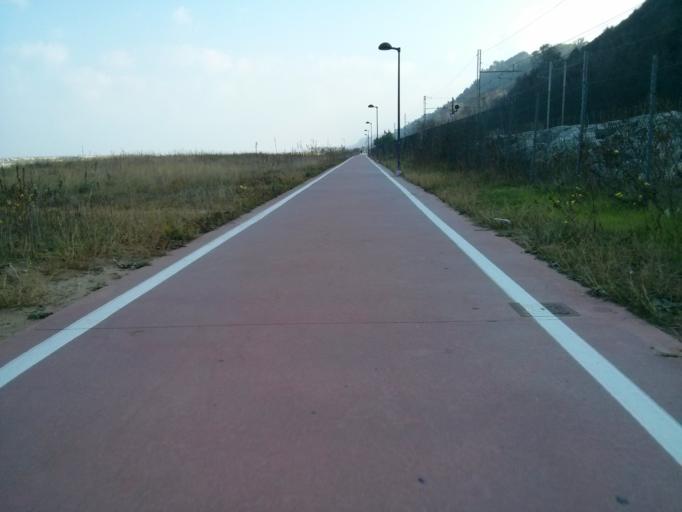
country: IT
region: The Marches
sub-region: Provincia di Pesaro e Urbino
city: Pesaro
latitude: 43.8961
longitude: 12.9429
